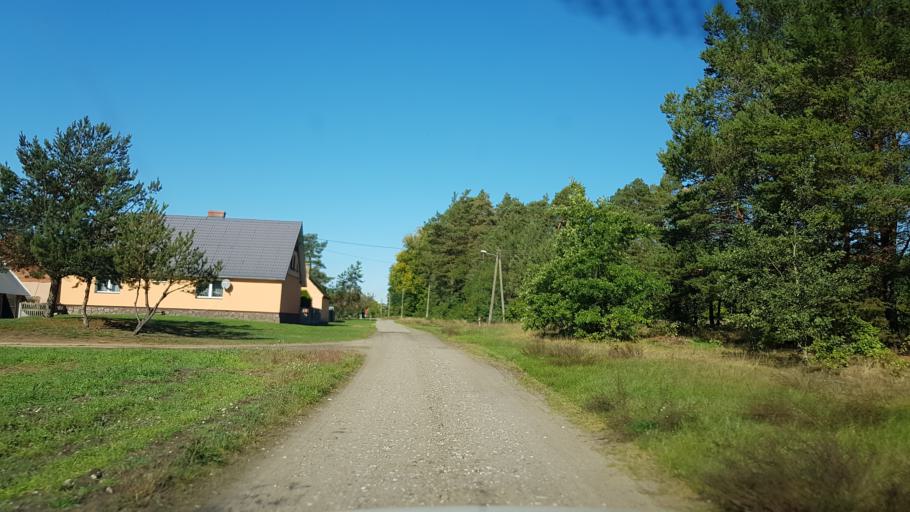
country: PL
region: Lubusz
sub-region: Powiat gorzowski
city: Lubiszyn
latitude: 52.8494
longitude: 14.9377
